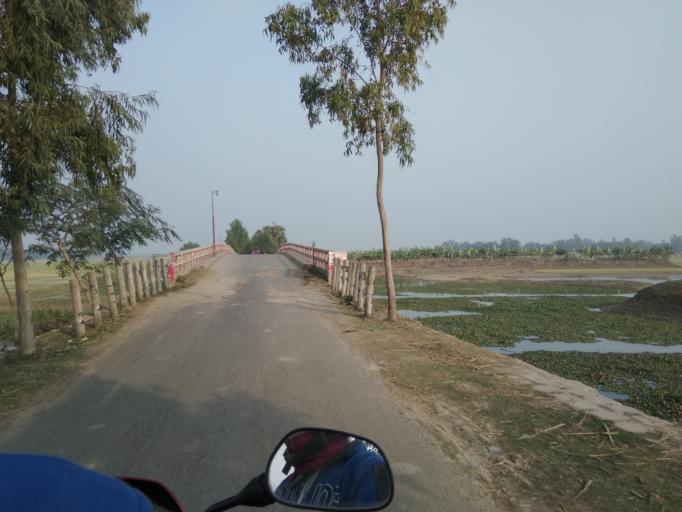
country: BD
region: Rajshahi
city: Par Naogaon
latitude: 24.4986
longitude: 89.1671
